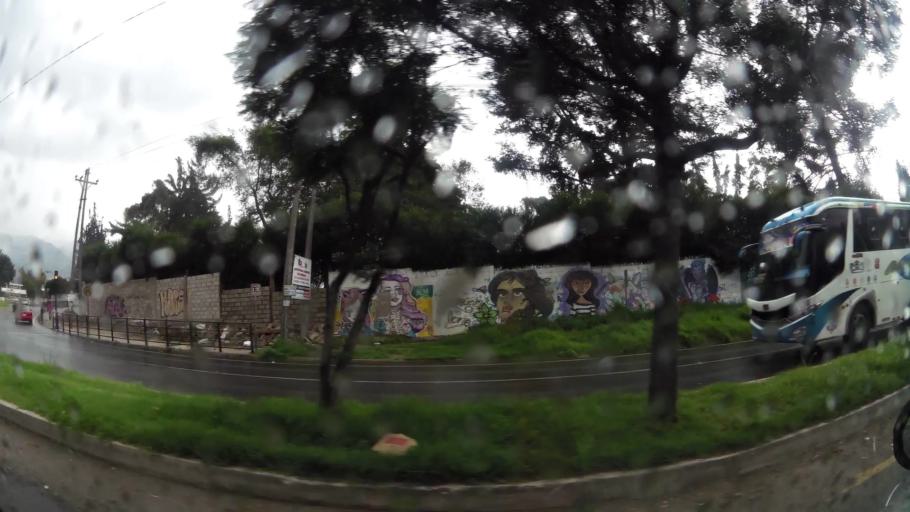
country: EC
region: Pichincha
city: Quito
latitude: -0.1009
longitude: -78.4906
